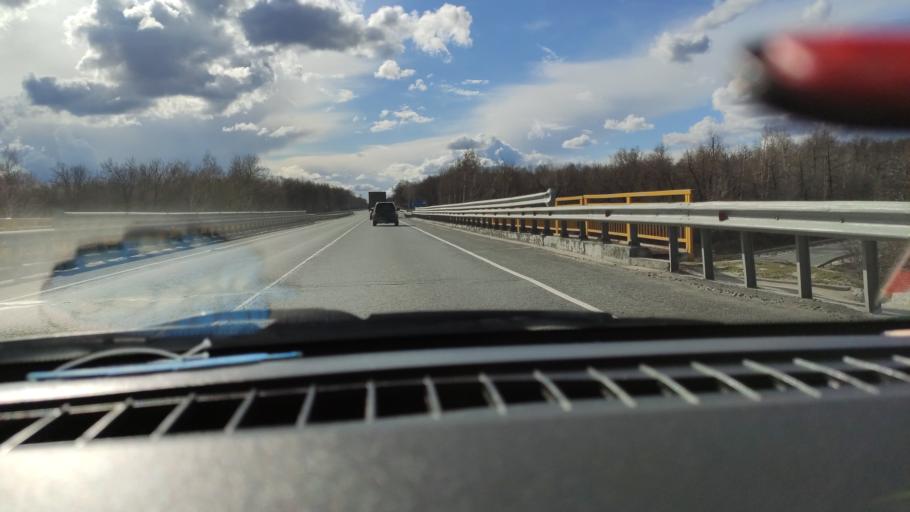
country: RU
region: Saratov
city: Vol'sk
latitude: 52.1094
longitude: 47.3741
